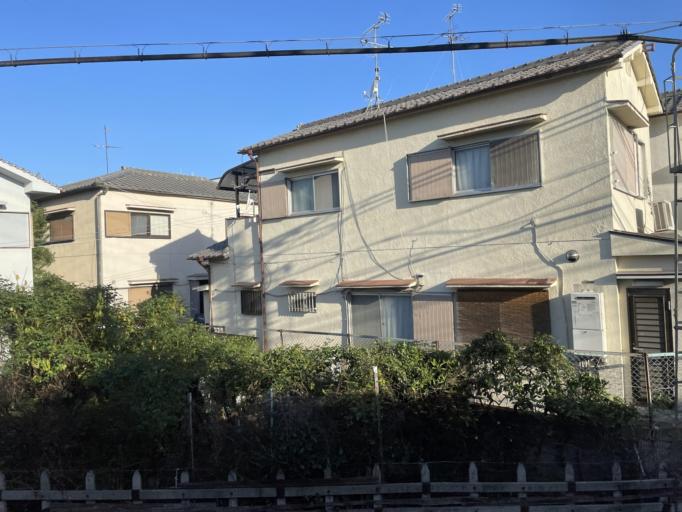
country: JP
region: Osaka
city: Kashihara
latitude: 34.5570
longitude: 135.6125
